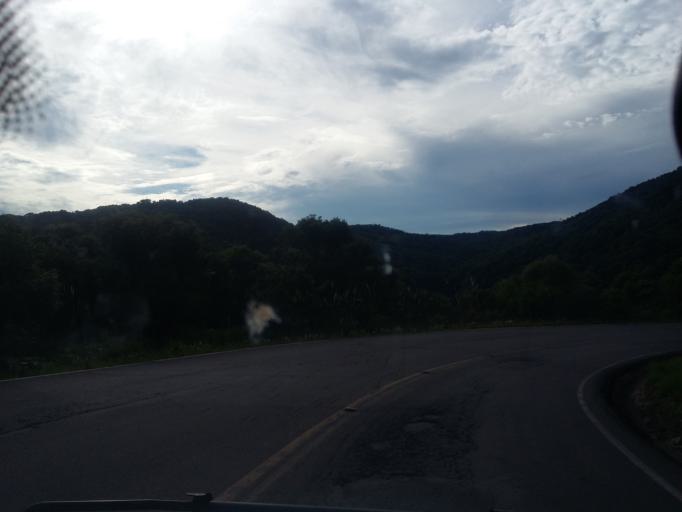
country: BR
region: Santa Catarina
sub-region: Celso Ramos
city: Celso Ramos
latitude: -27.6198
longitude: -51.4872
